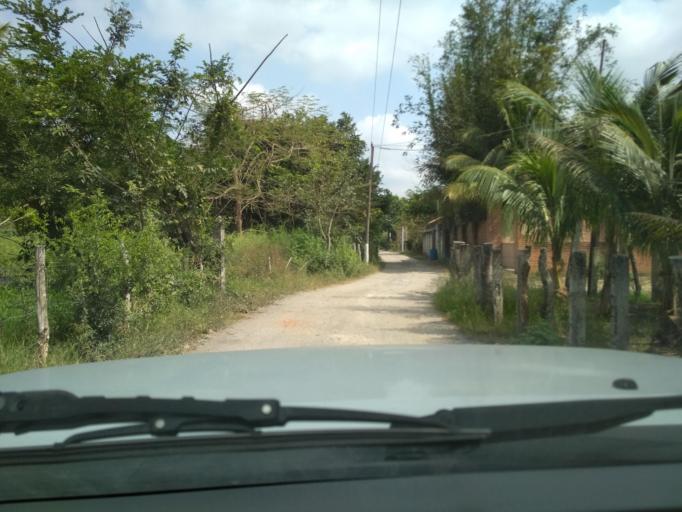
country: MX
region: Veracruz
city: El Tejar
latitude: 19.0787
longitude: -96.1701
